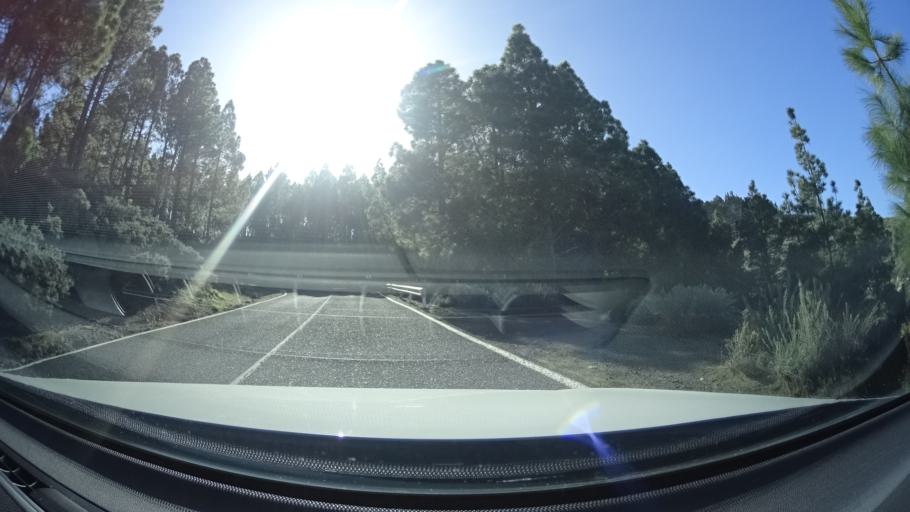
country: ES
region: Canary Islands
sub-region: Provincia de Las Palmas
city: Vega de San Mateo
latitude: 27.9652
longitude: -15.5406
